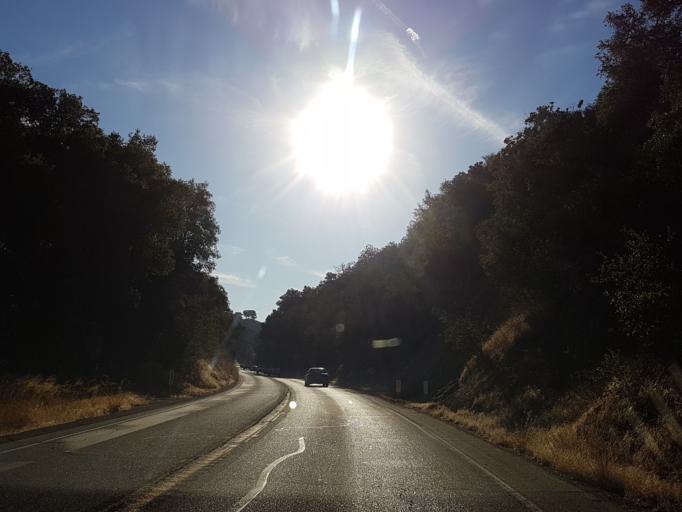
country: US
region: California
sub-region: Santa Barbara County
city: Goleta
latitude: 34.5589
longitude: -119.9168
